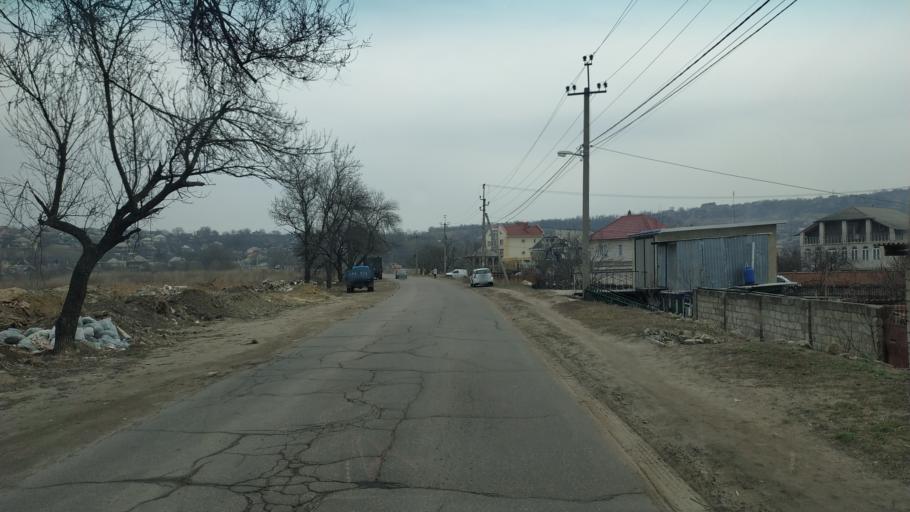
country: MD
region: Chisinau
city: Singera
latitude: 46.9178
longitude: 28.9768
